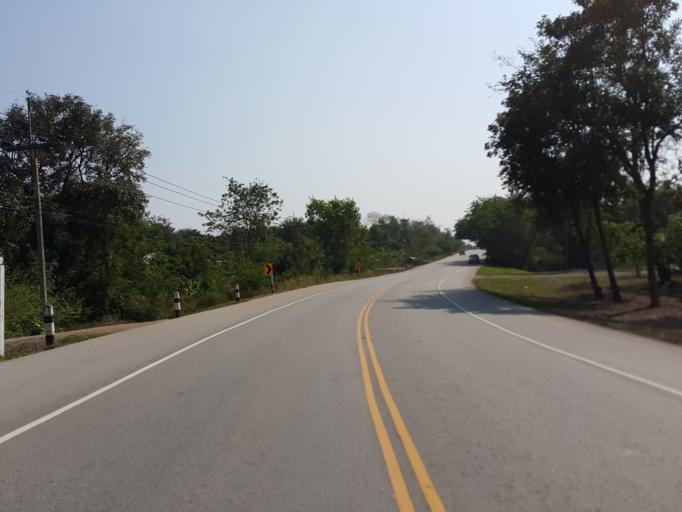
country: TH
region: Lampang
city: Mueang Pan
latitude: 18.9365
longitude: 99.6117
